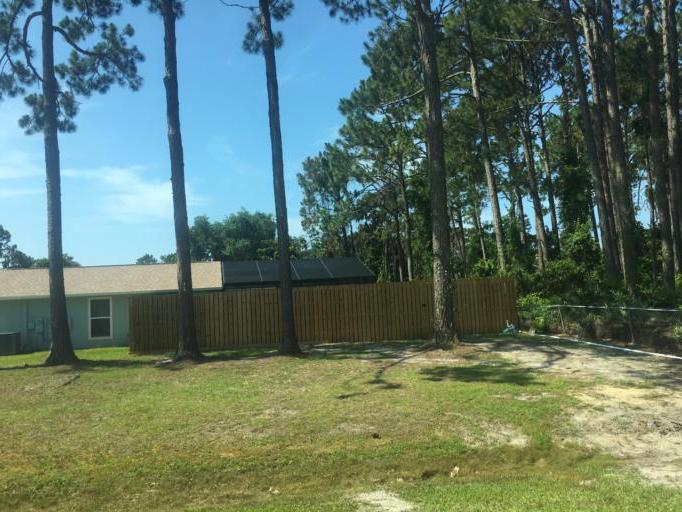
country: US
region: Florida
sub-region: Bay County
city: Panama City Beach
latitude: 30.1726
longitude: -85.7839
